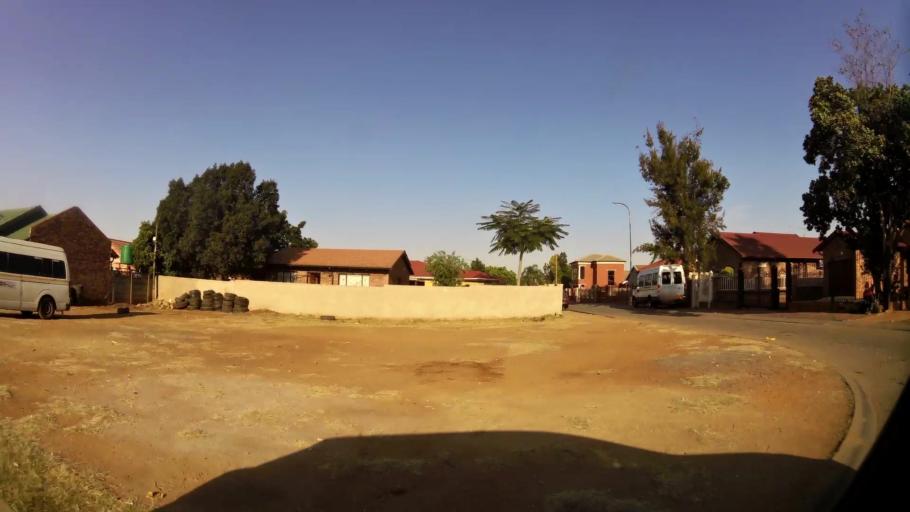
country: ZA
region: North-West
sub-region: Bojanala Platinum District Municipality
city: Rustenburg
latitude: -25.6512
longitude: 27.2178
